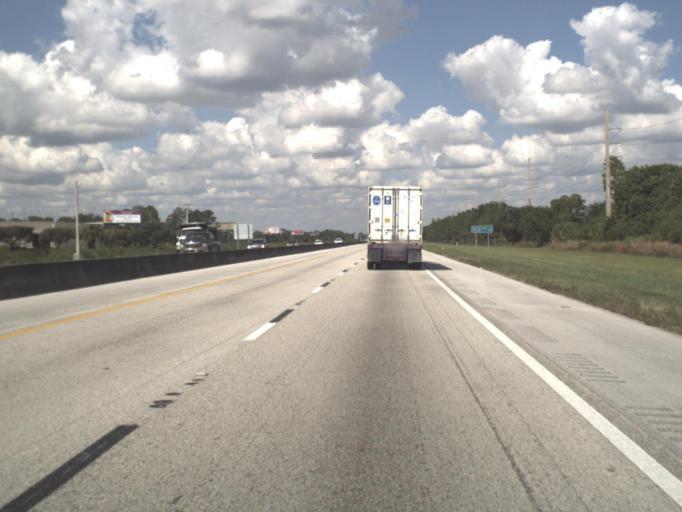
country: US
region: Florida
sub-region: Martin County
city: Palm City
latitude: 27.1666
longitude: -80.3081
